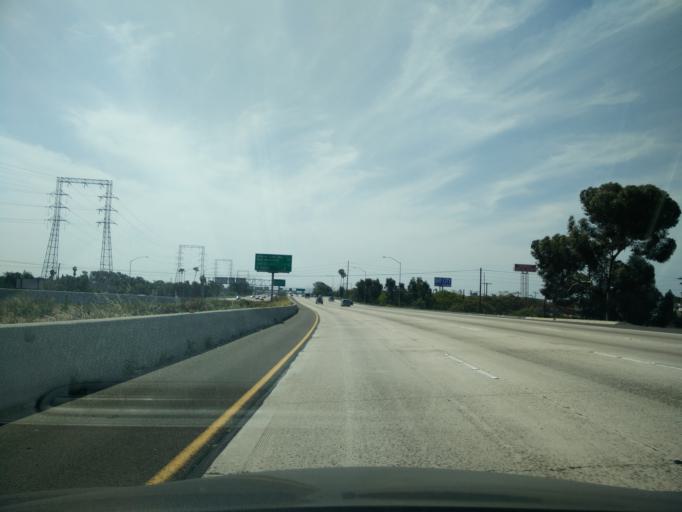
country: US
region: California
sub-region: San Diego County
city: National City
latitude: 32.6680
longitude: -117.1113
